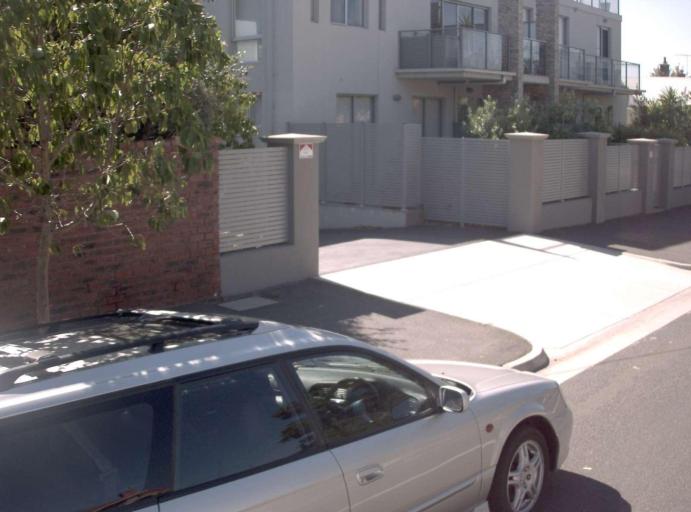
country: AU
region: Victoria
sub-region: Bayside
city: Hampton
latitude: -37.9416
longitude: 145.0017
